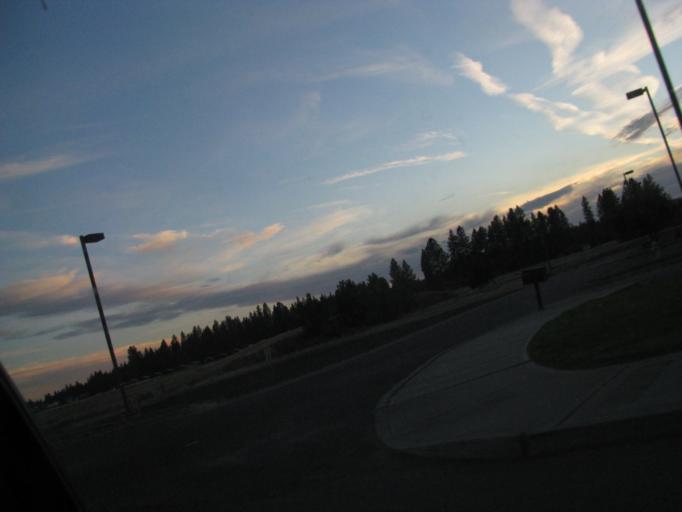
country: US
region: Washington
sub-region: Spokane County
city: Mead
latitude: 47.7900
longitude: -117.3525
